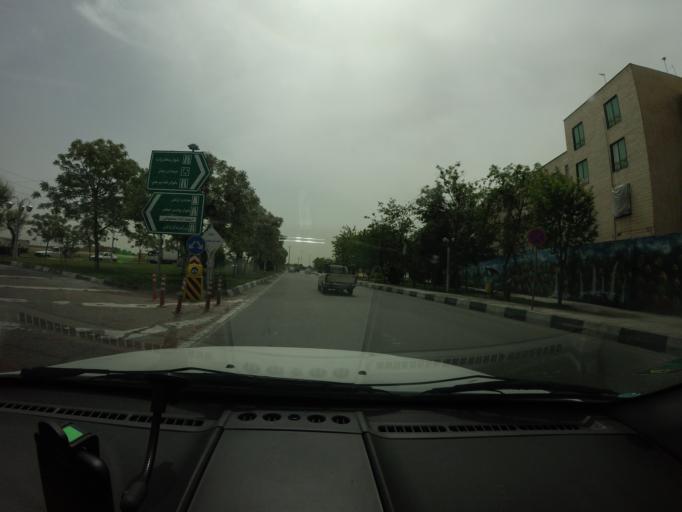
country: IR
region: Tehran
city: Eslamshahr
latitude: 35.5717
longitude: 51.2459
